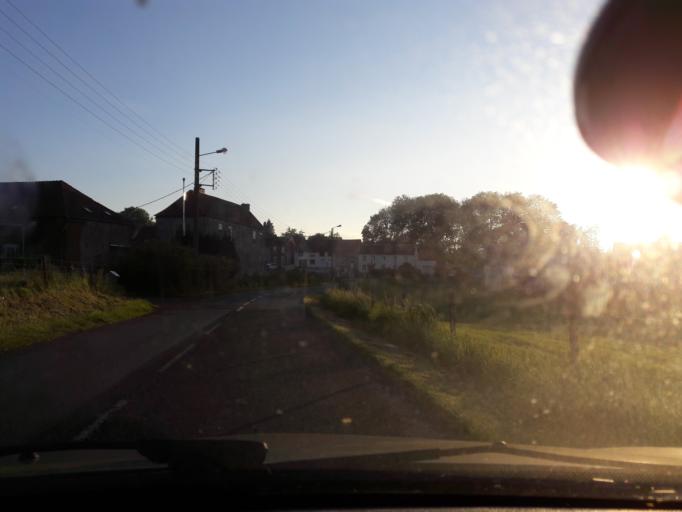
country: FR
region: Nord-Pas-de-Calais
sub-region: Departement du Nord
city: Marpent
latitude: 50.2842
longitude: 4.0693
